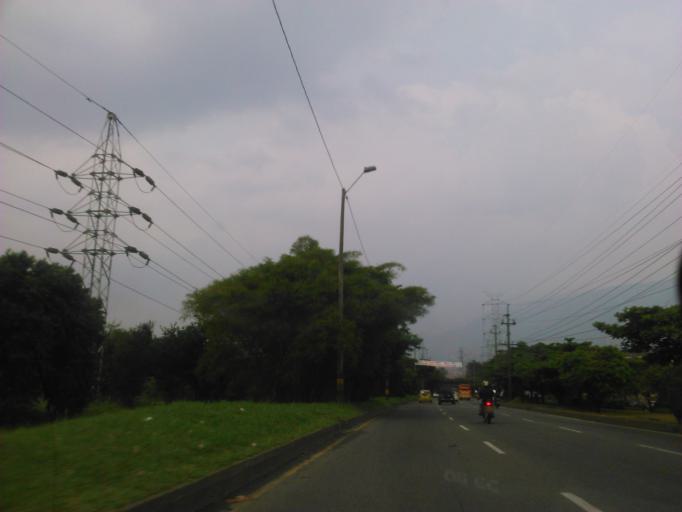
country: CO
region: Antioquia
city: Envigado
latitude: 6.1723
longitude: -75.5996
